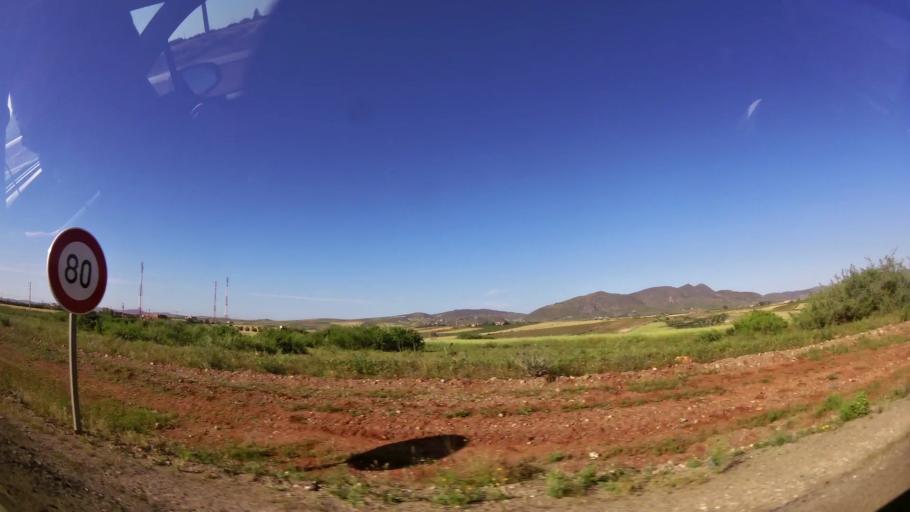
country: MA
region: Oriental
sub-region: Berkane-Taourirt
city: Ahfir
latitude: 34.9850
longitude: -2.1460
